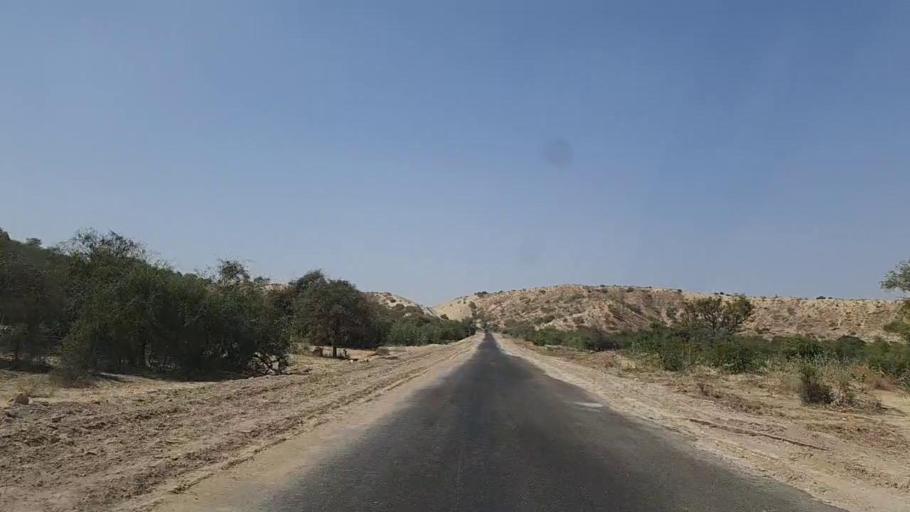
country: PK
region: Sindh
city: Diplo
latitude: 24.5843
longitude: 69.5220
